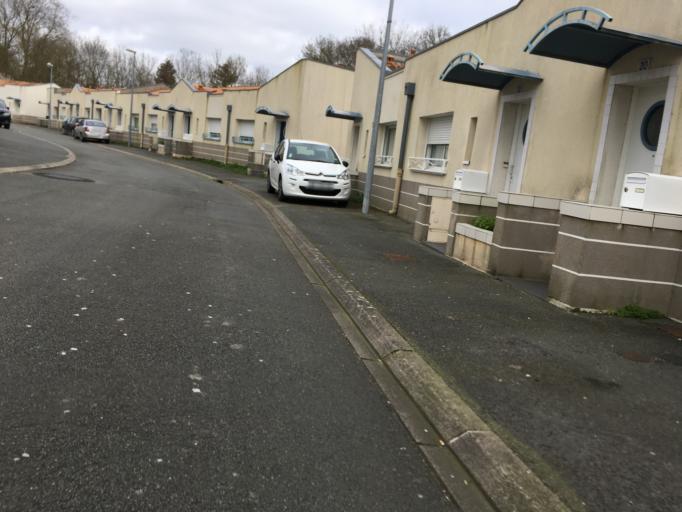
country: FR
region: Poitou-Charentes
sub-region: Departement de la Charente-Maritime
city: La Rochelle
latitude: 46.1755
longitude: -1.1456
